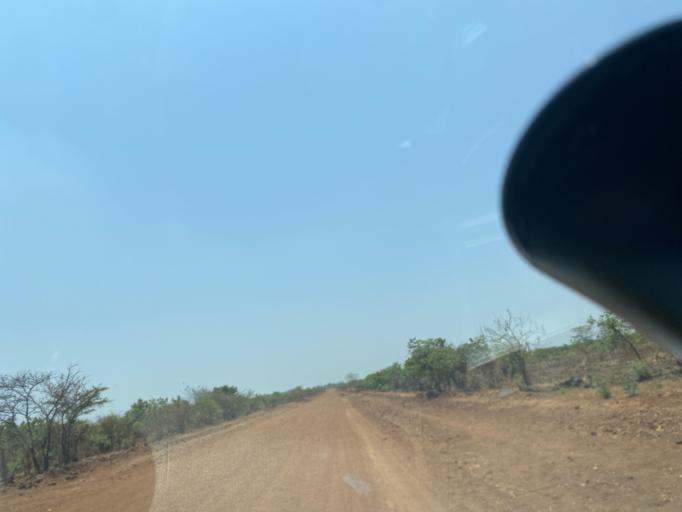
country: ZM
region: Lusaka
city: Lusaka
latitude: -15.4564
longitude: 27.9389
